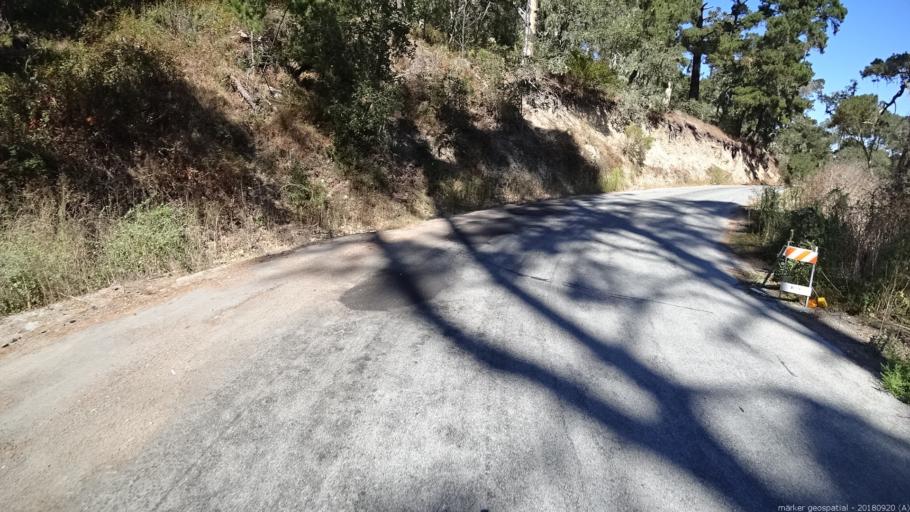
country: US
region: California
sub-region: Monterey County
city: Monterey
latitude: 36.5736
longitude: -121.8957
